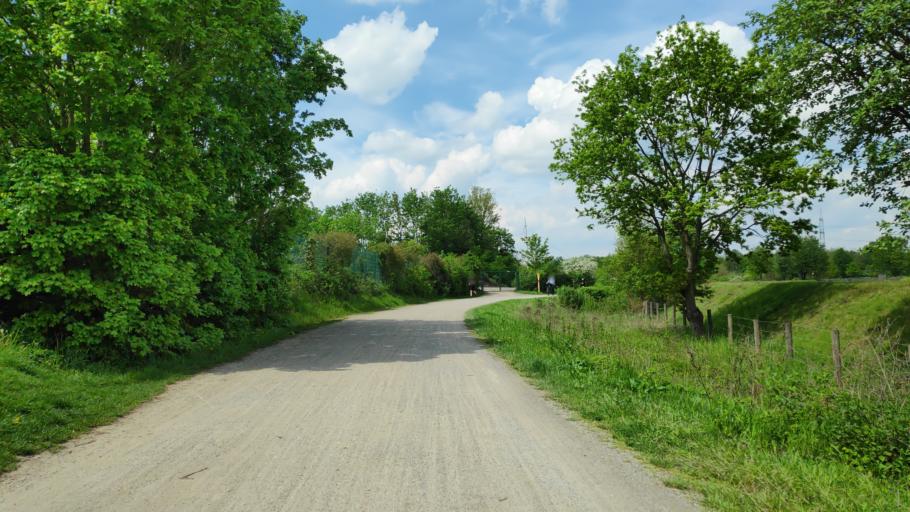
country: DE
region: North Rhine-Westphalia
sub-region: Regierungsbezirk Munster
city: Gelsenkirchen
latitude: 51.5447
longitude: 7.1162
